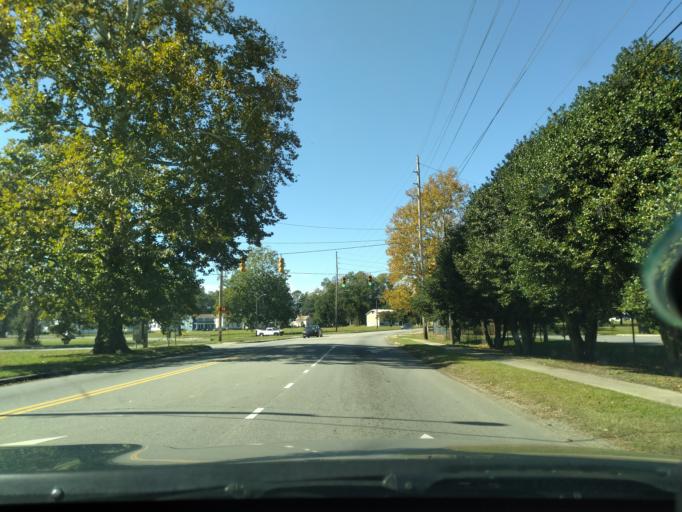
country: US
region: North Carolina
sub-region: Beaufort County
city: Washington
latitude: 35.5455
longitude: -77.0475
